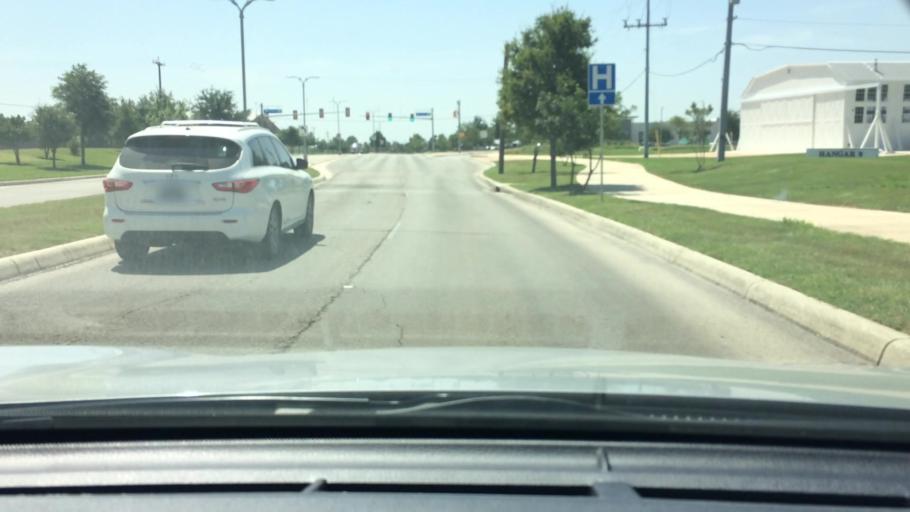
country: US
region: Texas
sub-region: Bexar County
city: San Antonio
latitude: 29.3449
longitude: -98.4445
